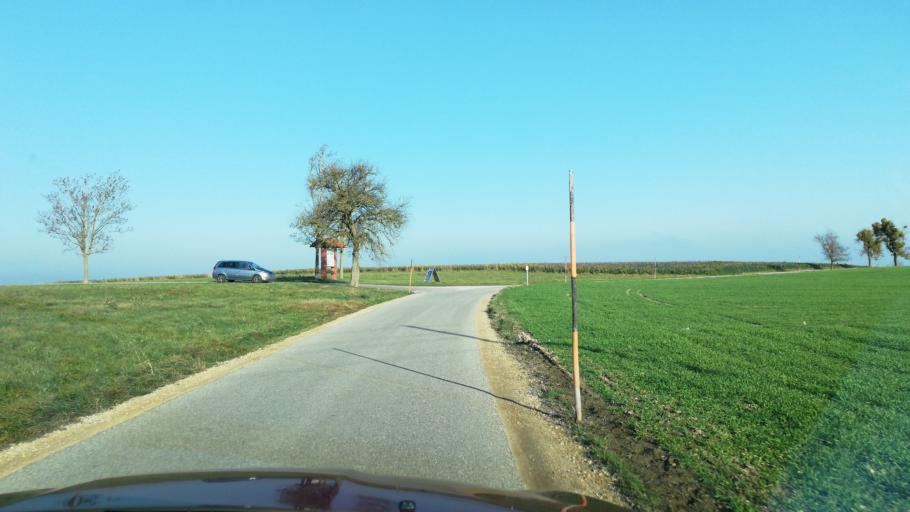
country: AT
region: Upper Austria
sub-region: Wels-Land
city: Buchkirchen
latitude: 48.2685
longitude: 14.0116
